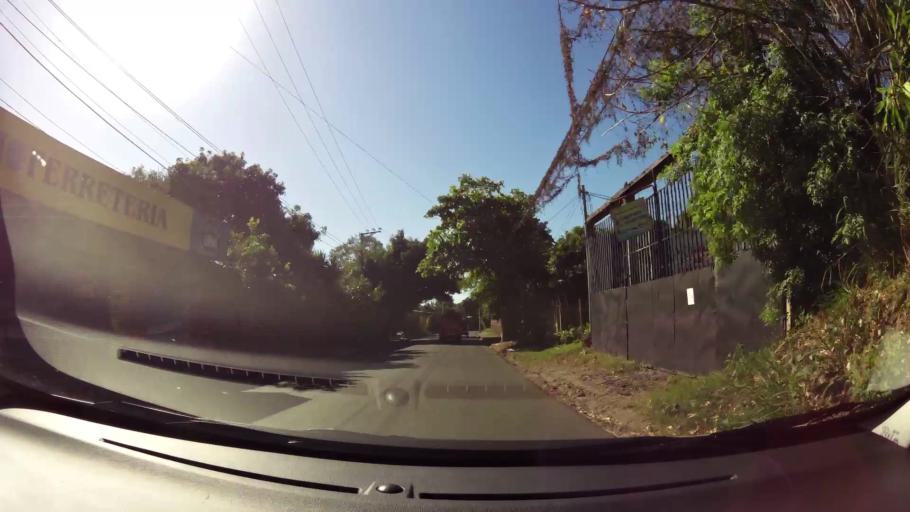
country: SV
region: Sonsonate
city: Sonzacate
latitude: 13.7339
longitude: -89.7193
